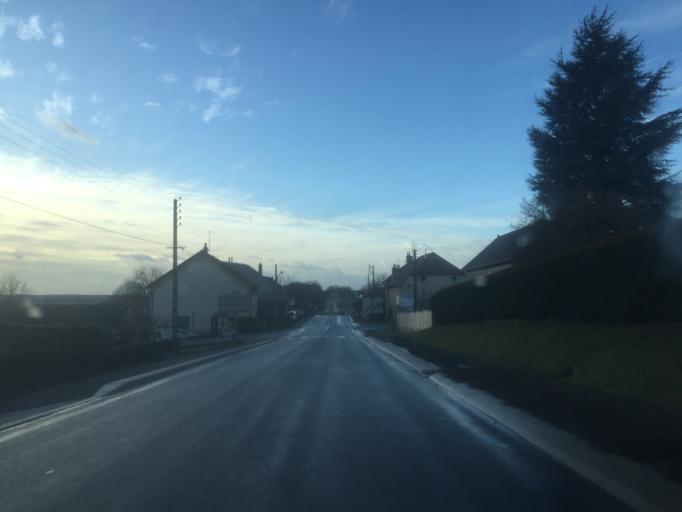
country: FR
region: Franche-Comte
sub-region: Departement du Jura
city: Dampierre
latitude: 47.1511
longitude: 5.7228
